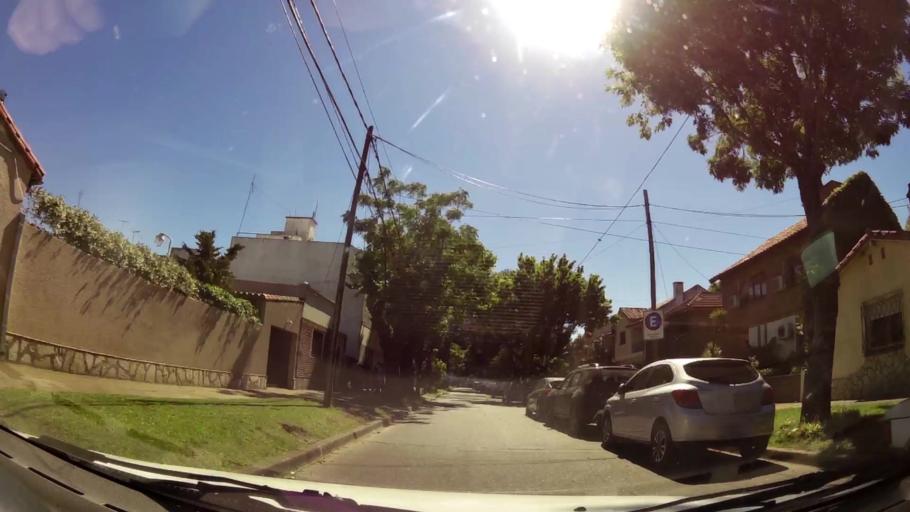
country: AR
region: Buenos Aires
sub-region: Partido de Vicente Lopez
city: Olivos
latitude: -34.5203
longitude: -58.4906
